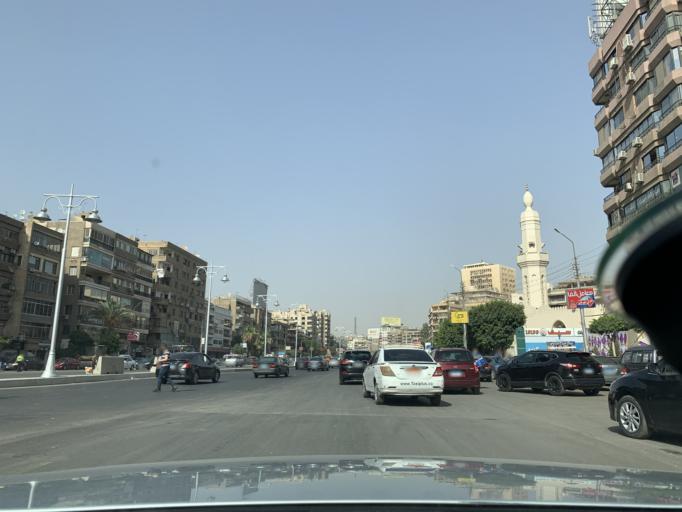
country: EG
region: Muhafazat al Qahirah
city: Cairo
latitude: 30.0842
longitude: 31.3273
